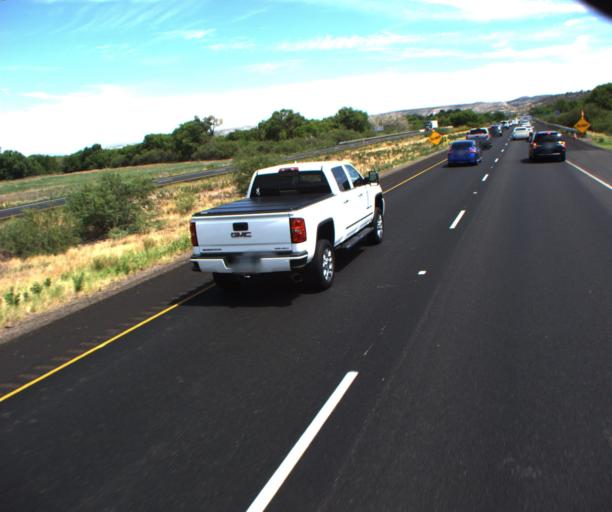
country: US
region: Arizona
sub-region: Yavapai County
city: Camp Verde
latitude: 34.5839
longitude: -111.8807
